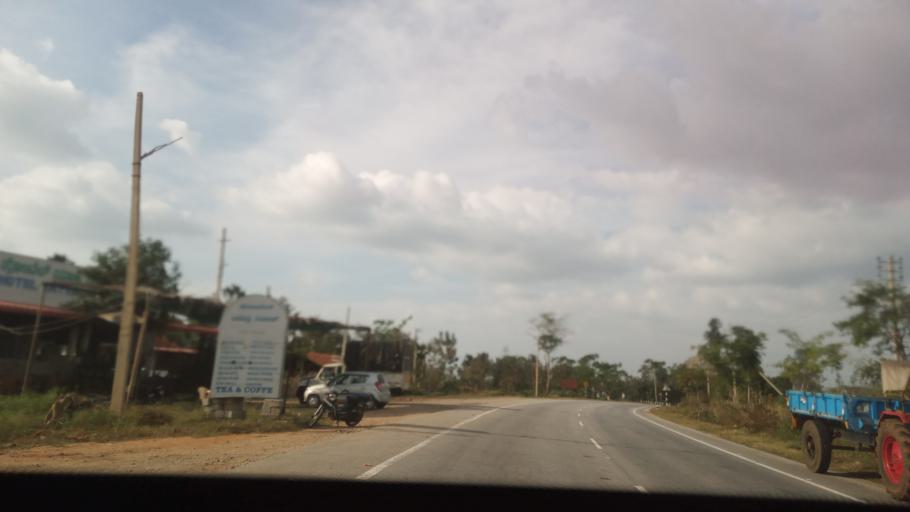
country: IN
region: Karnataka
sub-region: Mandya
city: Maddur
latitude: 12.8011
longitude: 77.0383
